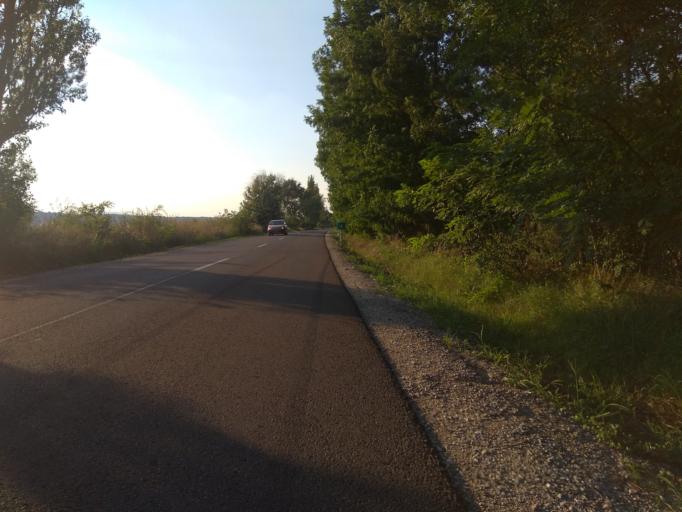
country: HU
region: Borsod-Abauj-Zemplen
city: Nyekladhaza
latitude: 47.9680
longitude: 20.8559
